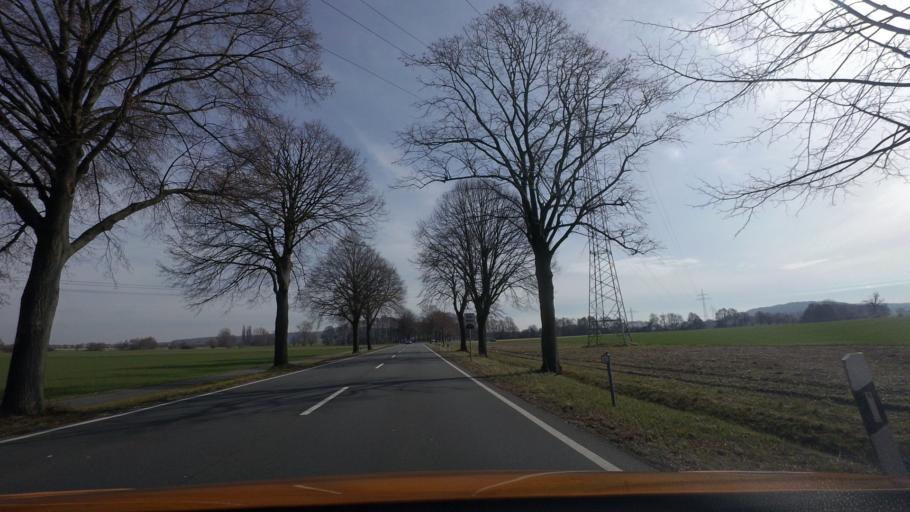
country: DE
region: Lower Saxony
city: Gehrden
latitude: 52.3402
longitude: 9.5599
